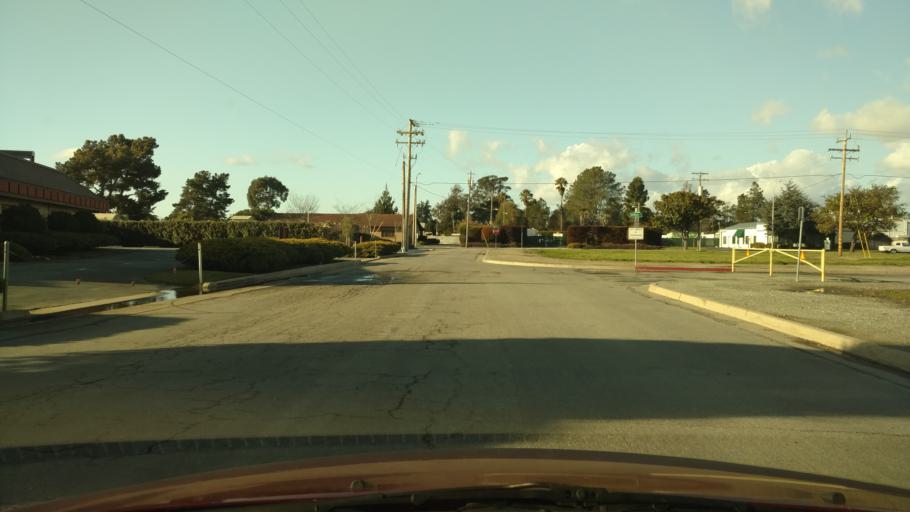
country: US
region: California
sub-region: Monterey County
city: Salinas
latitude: 36.6648
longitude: -121.6158
